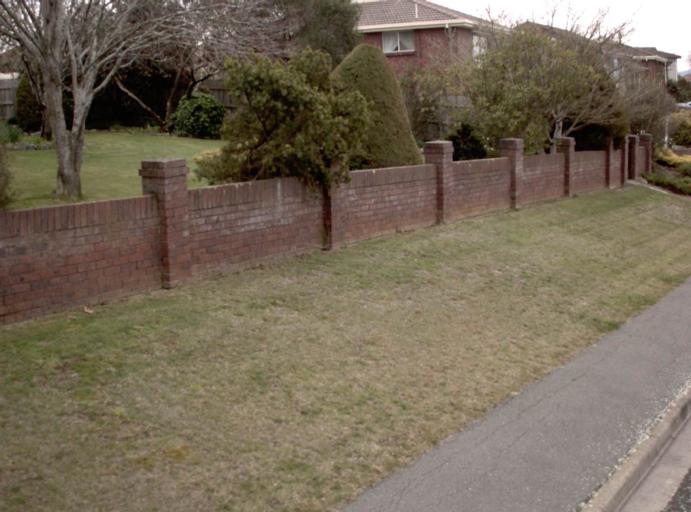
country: AU
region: Tasmania
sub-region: Launceston
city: Newstead
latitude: -41.4610
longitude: 147.1798
